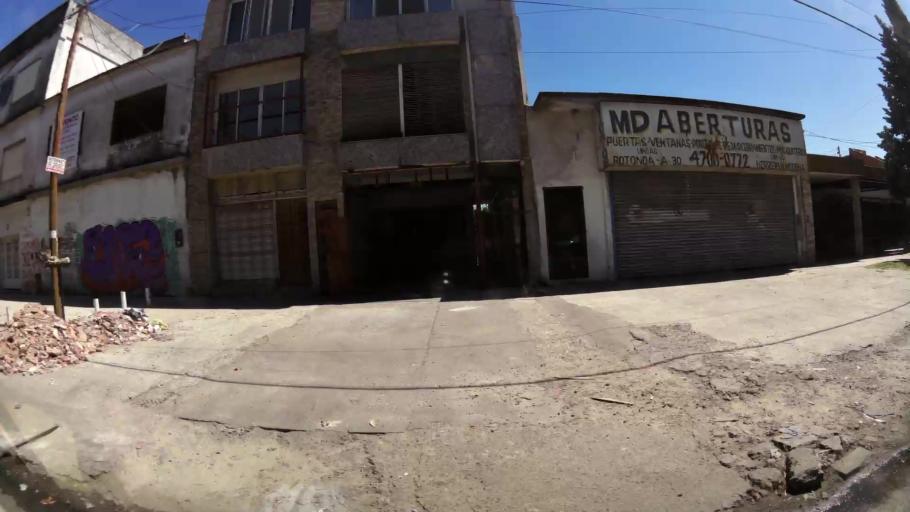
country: AR
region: Buenos Aires
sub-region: Partido de San Isidro
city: San Isidro
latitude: -34.5087
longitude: -58.5789
